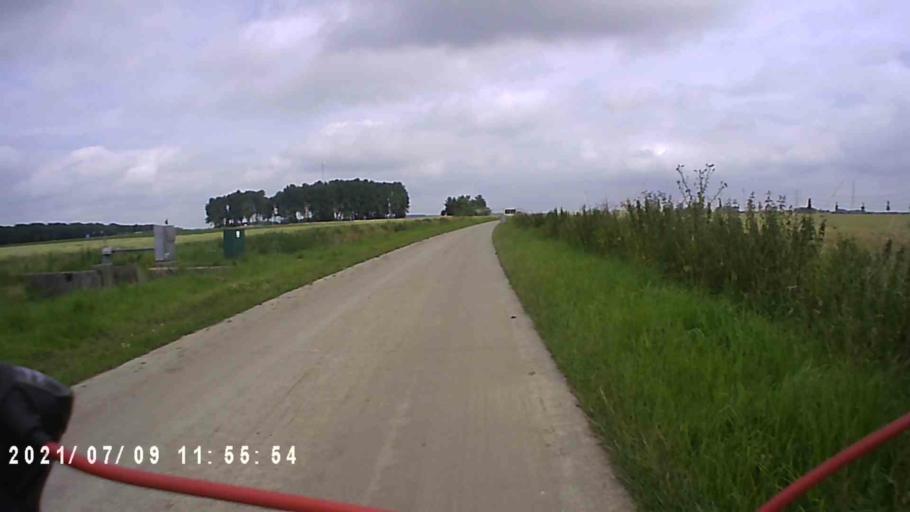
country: NL
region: Groningen
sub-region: Gemeente Veendam
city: Veendam
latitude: 53.1898
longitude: 6.9030
